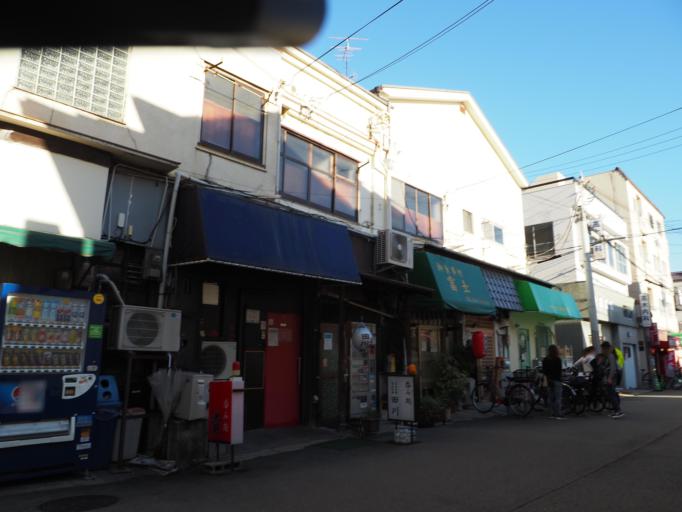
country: JP
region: Hyogo
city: Kobe
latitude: 34.6520
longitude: 135.1482
